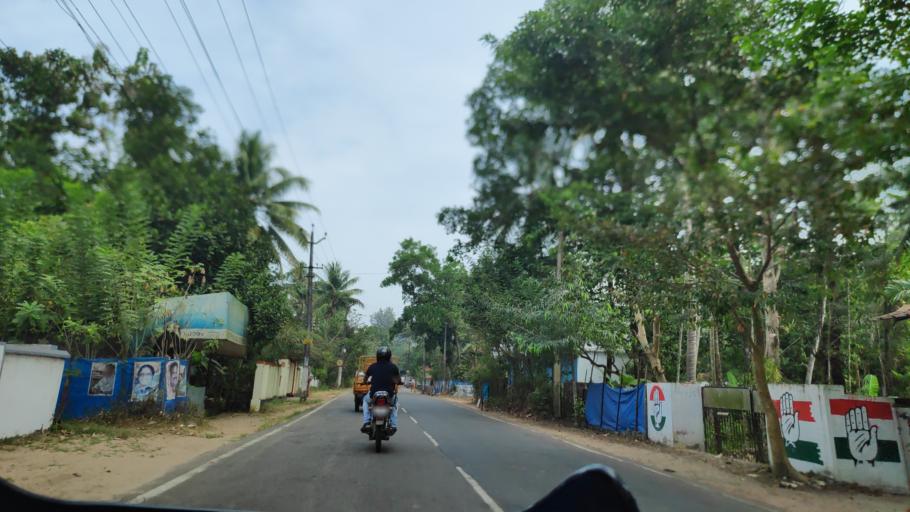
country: IN
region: Kerala
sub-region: Alappuzha
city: Vayalar
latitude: 9.7164
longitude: 76.3595
